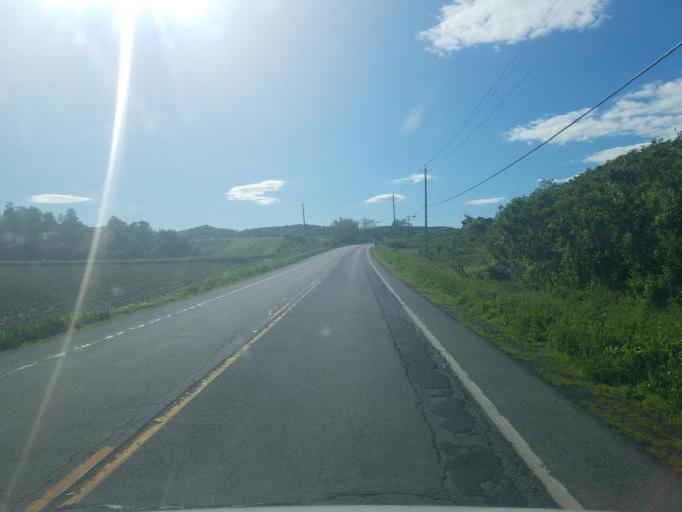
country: US
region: New York
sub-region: Herkimer County
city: Little Falls
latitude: 43.0153
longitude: -74.8073
